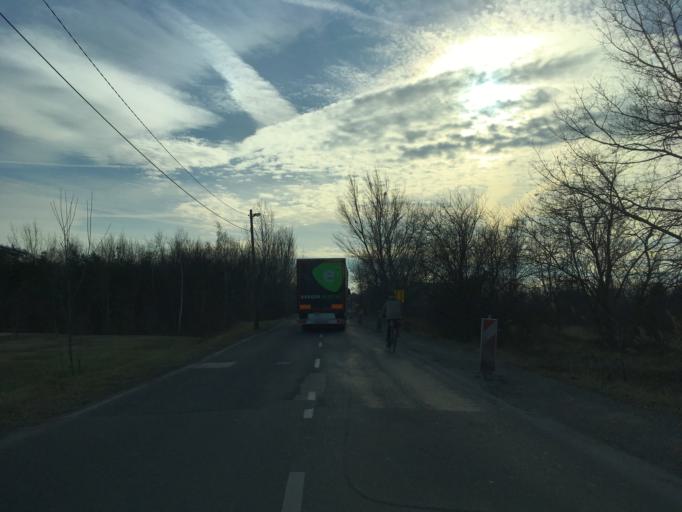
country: HU
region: Gyor-Moson-Sopron
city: Gyor
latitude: 47.6992
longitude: 17.6632
